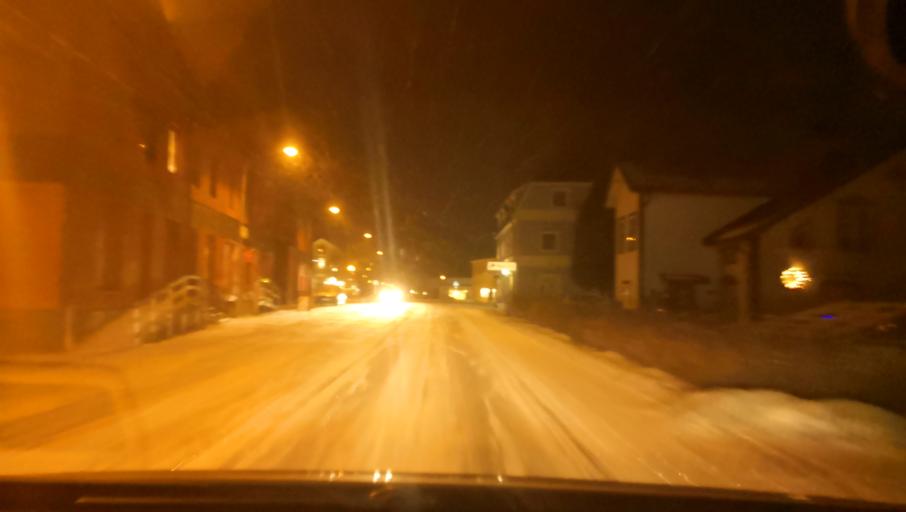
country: SE
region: Uppsala
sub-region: Heby Kommun
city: Tarnsjo
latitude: 60.1544
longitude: 16.9291
